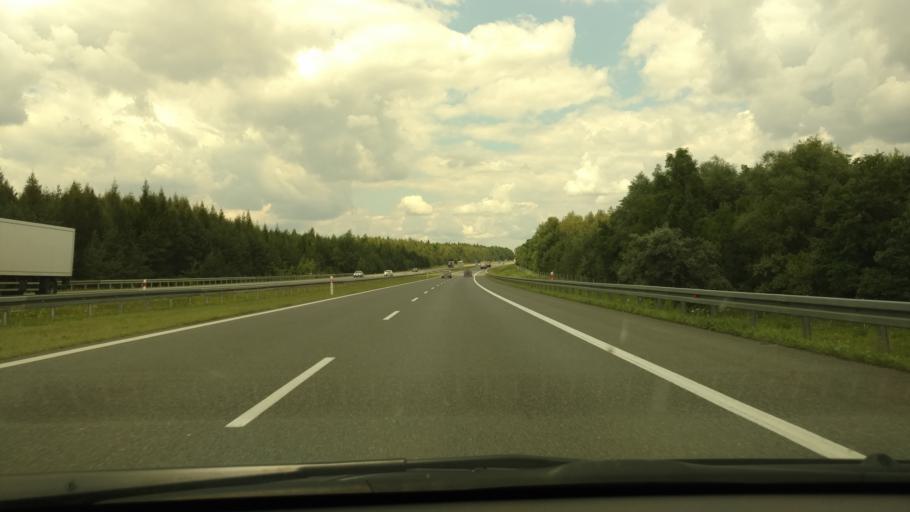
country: PL
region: Silesian Voivodeship
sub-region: Myslowice
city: Myslowice
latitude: 50.1843
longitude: 19.1937
